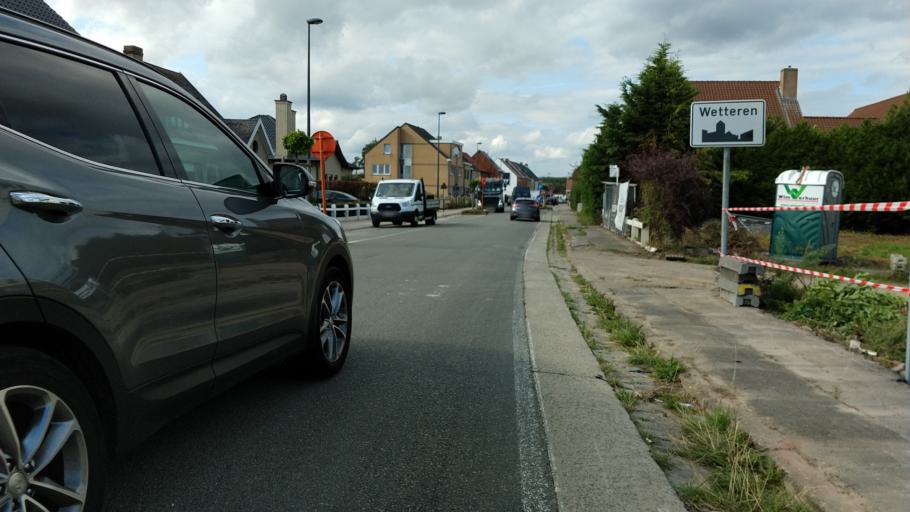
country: BE
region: Flanders
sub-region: Provincie Oost-Vlaanderen
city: Wetteren
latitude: 50.9967
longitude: 3.8597
